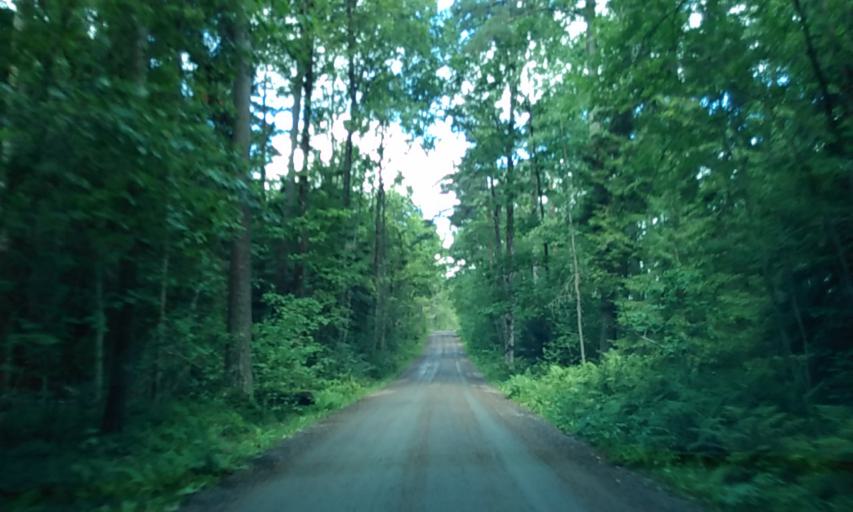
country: SE
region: Vaestra Goetaland
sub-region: Lerums Kommun
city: Grabo
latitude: 57.9078
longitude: 12.3753
